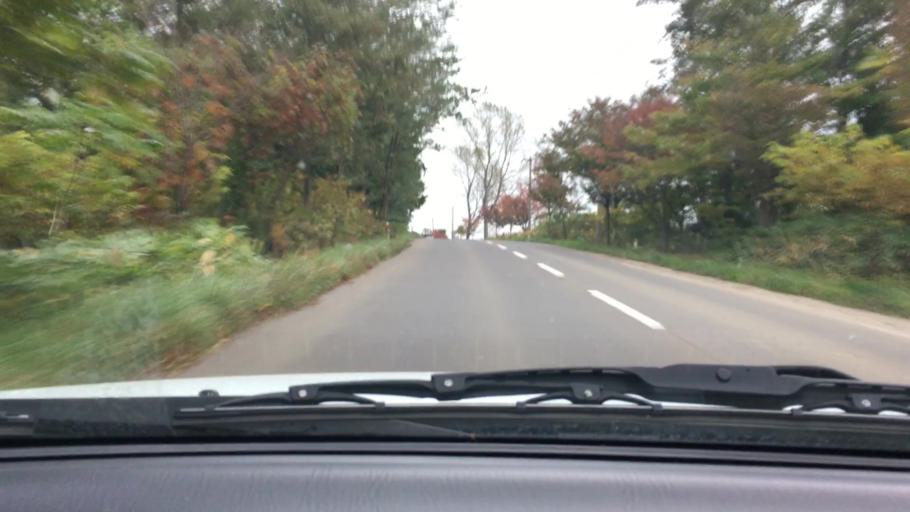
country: JP
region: Aomori
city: Shimokizukuri
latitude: 40.7170
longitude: 140.3116
